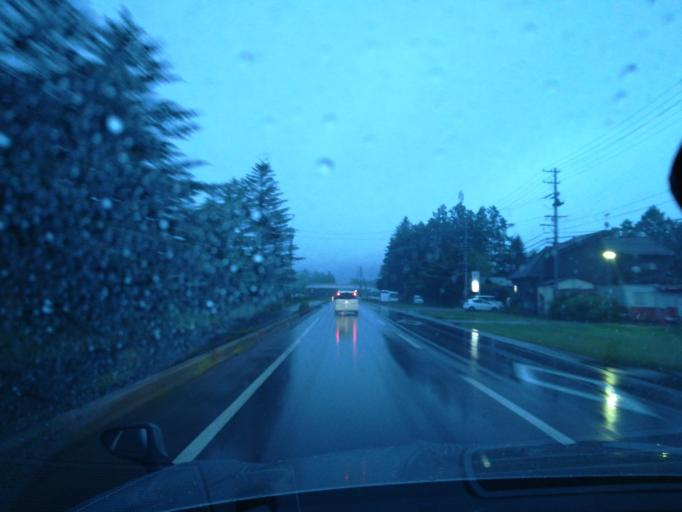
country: JP
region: Nagano
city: Saku
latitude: 36.3139
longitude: 138.6313
